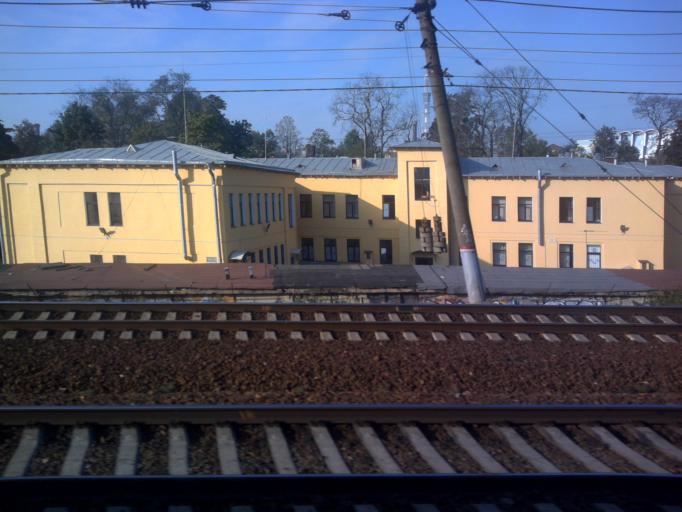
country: RU
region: Leningrad
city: Sampsonievskiy
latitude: 59.9795
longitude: 30.3420
